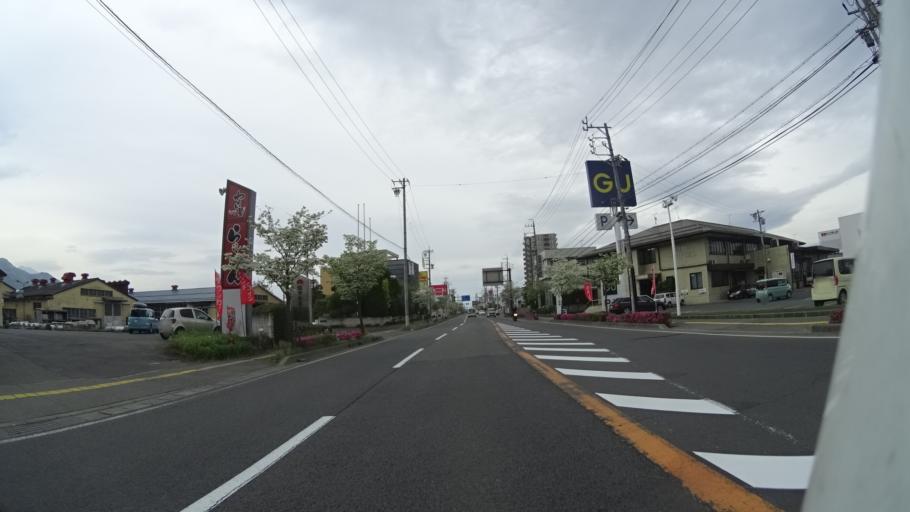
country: JP
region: Nagano
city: Nagano-shi
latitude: 36.6050
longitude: 138.1623
